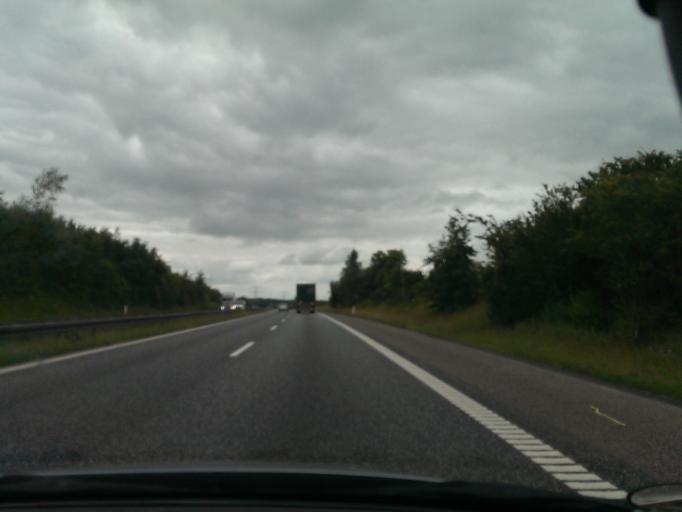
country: DK
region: Central Jutland
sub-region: Arhus Kommune
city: Trige
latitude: 56.2363
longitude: 10.1254
